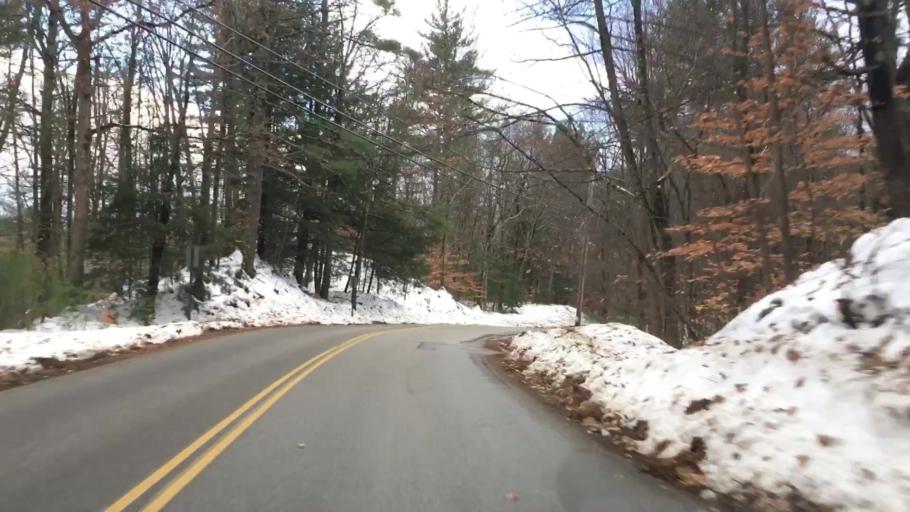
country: US
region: New Hampshire
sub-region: Hillsborough County
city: Mont Vernon
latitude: 42.8997
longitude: -71.6035
